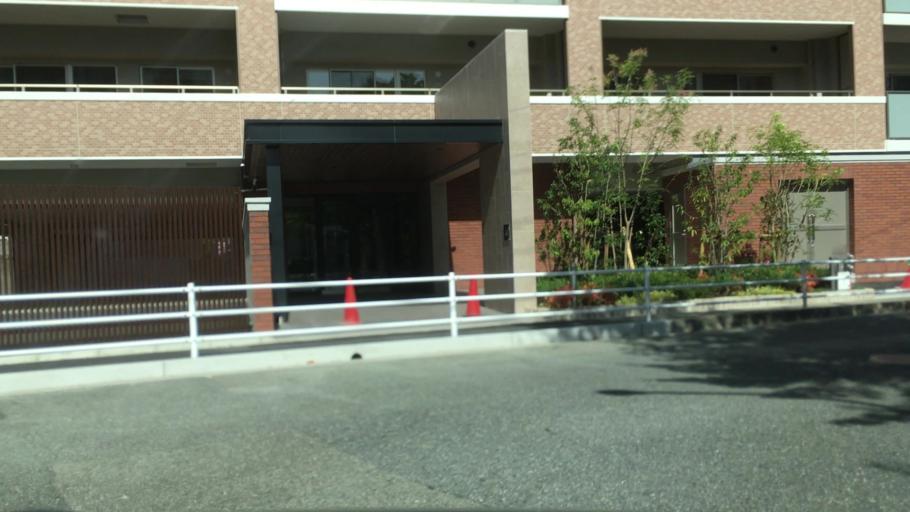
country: JP
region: Fukuoka
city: Fukuoka-shi
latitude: 33.5736
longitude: 130.3739
